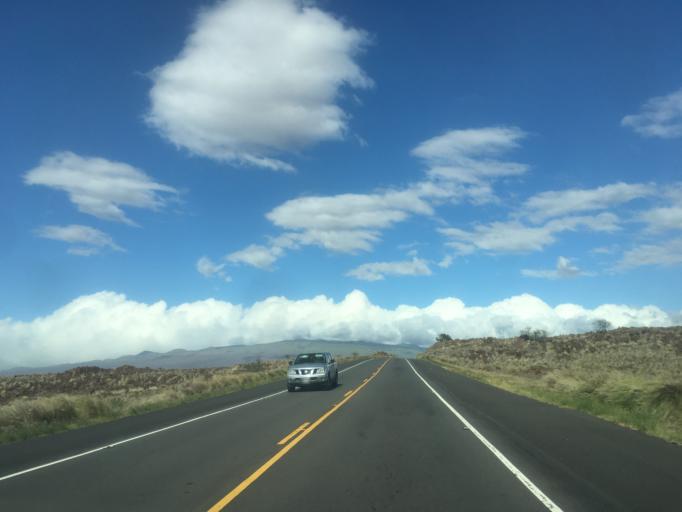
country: US
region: Hawaii
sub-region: Hawaii County
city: Waikoloa
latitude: 19.9184
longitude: -155.8049
